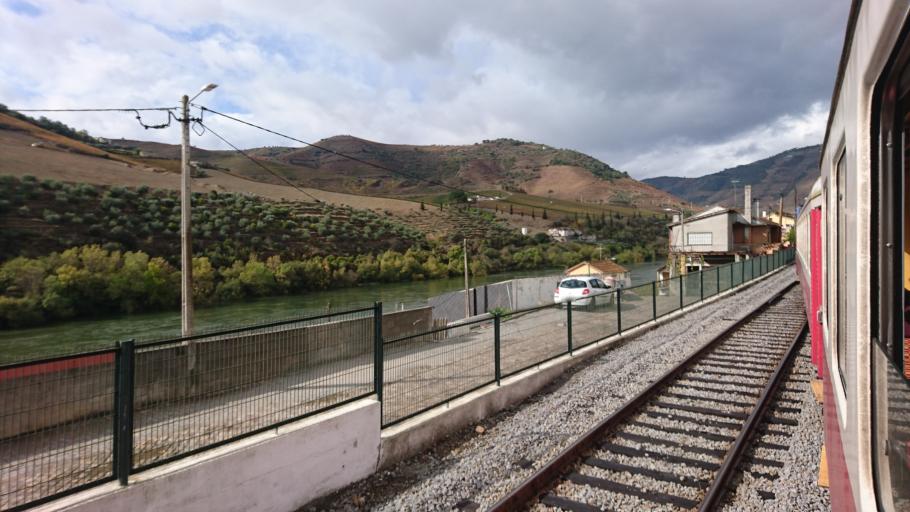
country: PT
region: Viseu
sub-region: Sao Joao da Pesqueira
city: Sao Joao da Pesqueira
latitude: 41.2080
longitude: -7.4221
